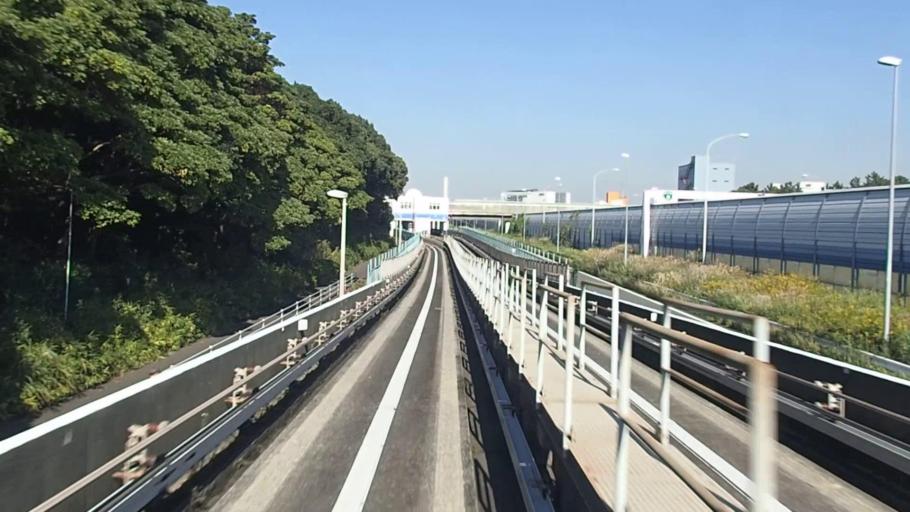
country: JP
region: Kanagawa
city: Yokohama
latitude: 35.3701
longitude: 139.6428
